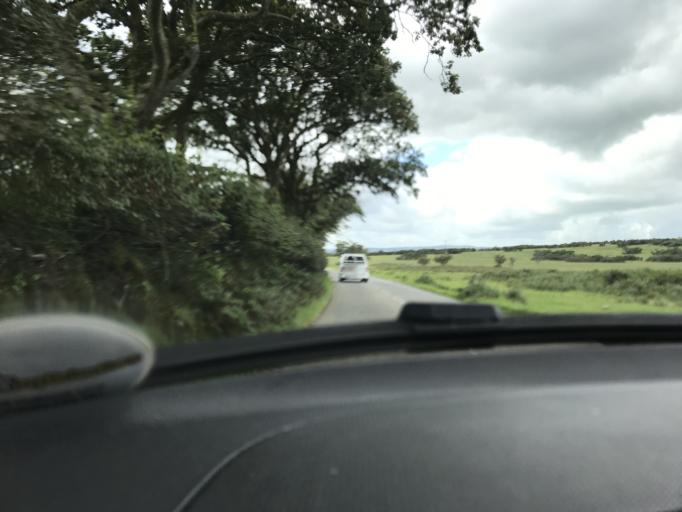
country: GB
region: England
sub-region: Devon
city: Horrabridge
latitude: 50.5417
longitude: -4.1013
